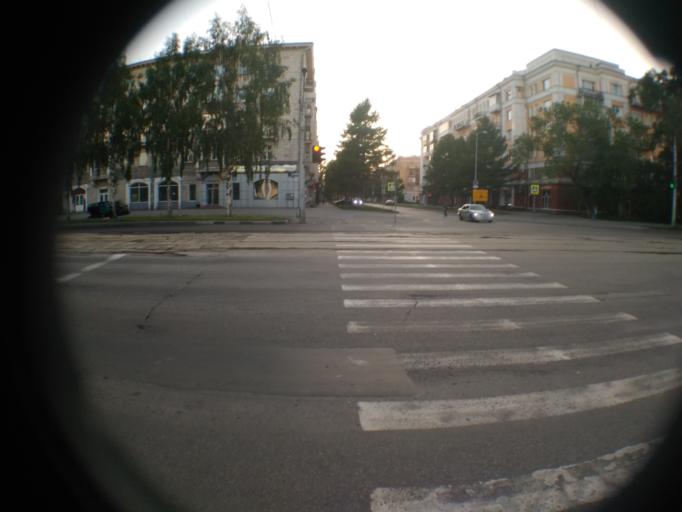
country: RU
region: Kemerovo
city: Novokuznetsk
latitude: 53.7545
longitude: 87.1185
